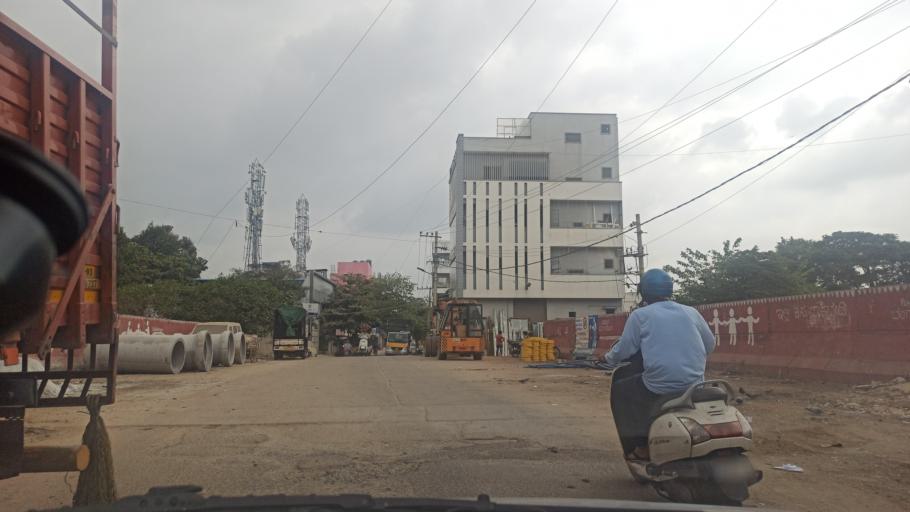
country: IN
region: Karnataka
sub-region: Bangalore Urban
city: Yelahanka
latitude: 13.0460
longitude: 77.6012
